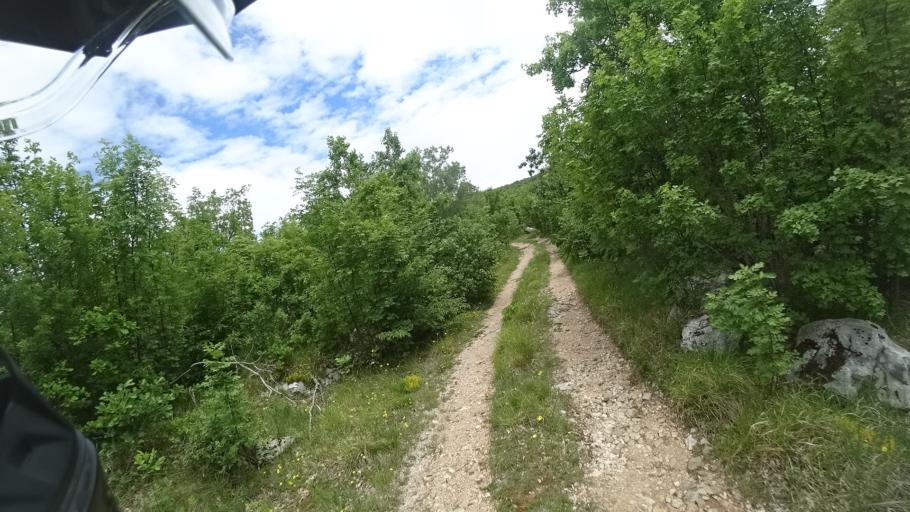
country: HR
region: Splitsko-Dalmatinska
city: Hrvace
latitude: 43.8837
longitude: 16.5826
